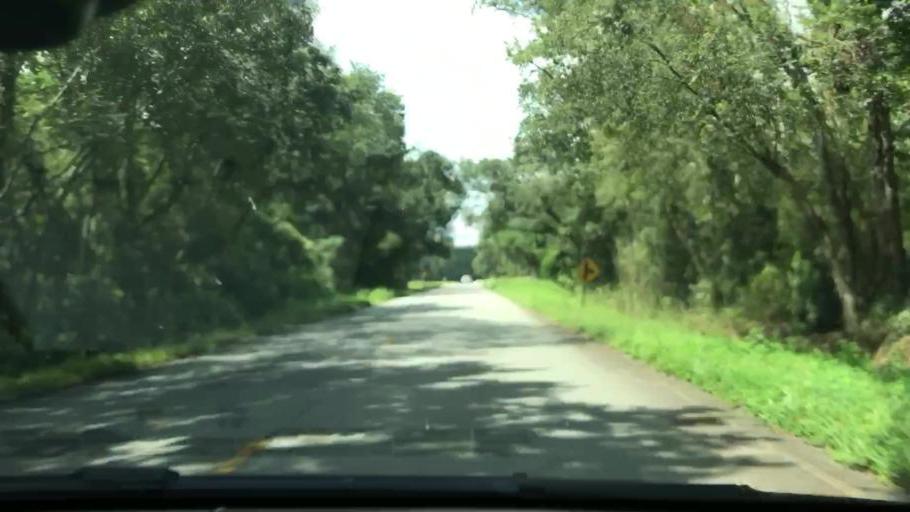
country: US
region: Georgia
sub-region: Seminole County
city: Donalsonville
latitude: 30.9881
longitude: -84.9780
